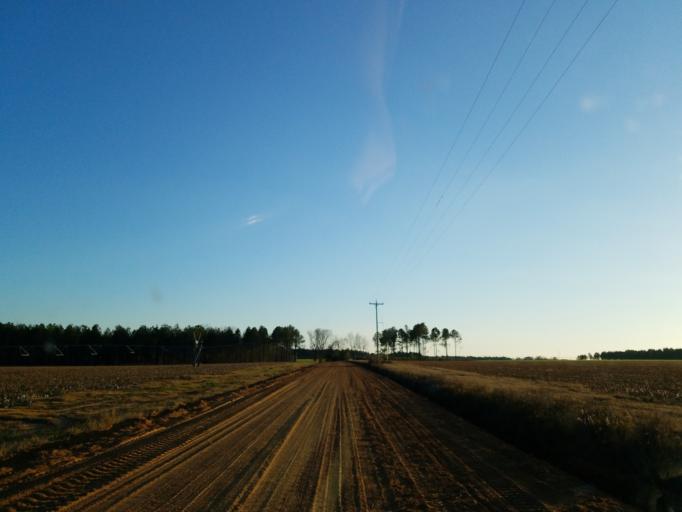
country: US
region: Georgia
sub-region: Worth County
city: Sylvester
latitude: 31.5936
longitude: -83.7878
